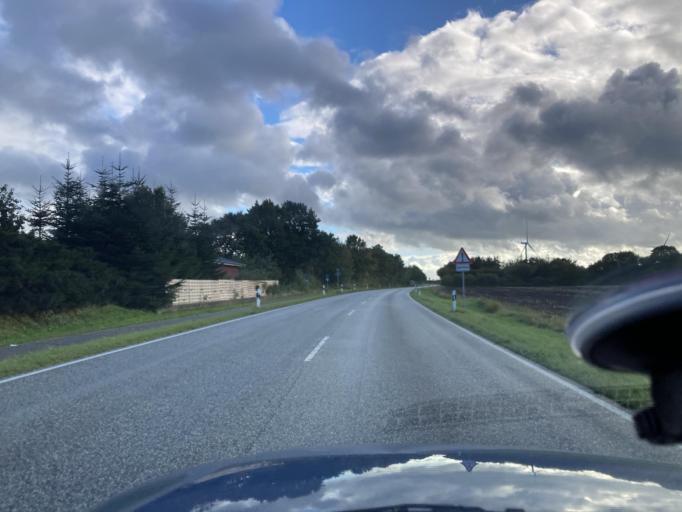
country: DE
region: Schleswig-Holstein
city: Hamdorf
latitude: 54.2523
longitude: 9.5328
